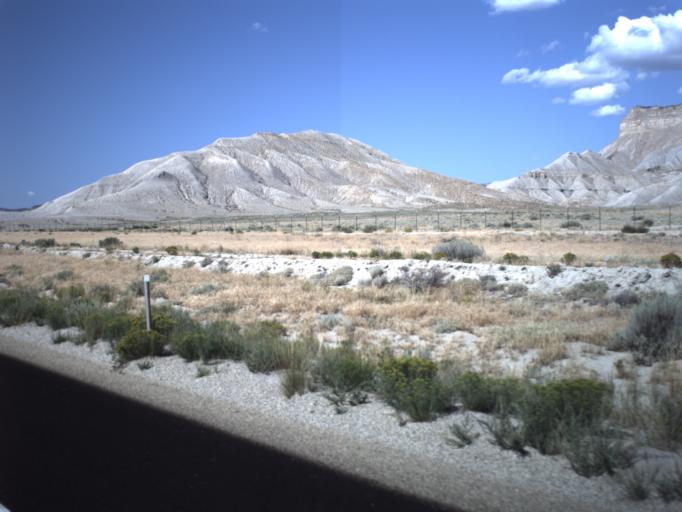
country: US
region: Utah
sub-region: Emery County
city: Ferron
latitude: 39.0075
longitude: -111.1539
